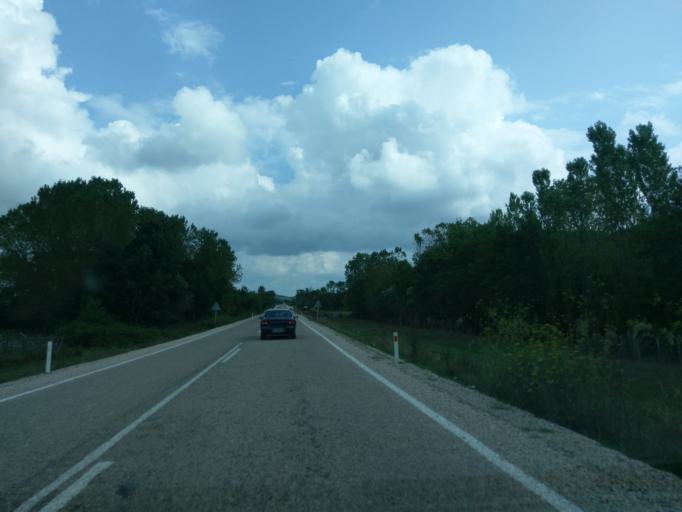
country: TR
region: Sinop
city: Erfelek
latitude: 42.0219
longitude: 34.9855
